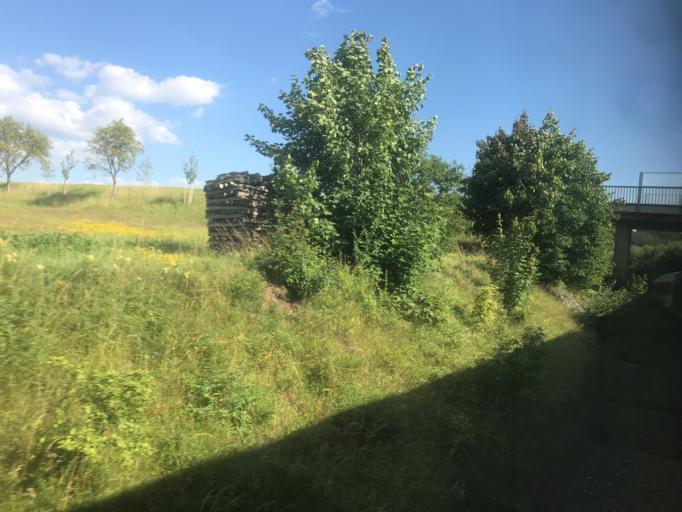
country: AT
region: Upper Austria
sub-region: Politischer Bezirk Urfahr-Umgebung
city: Reichenthal
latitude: 48.5519
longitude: 14.4372
